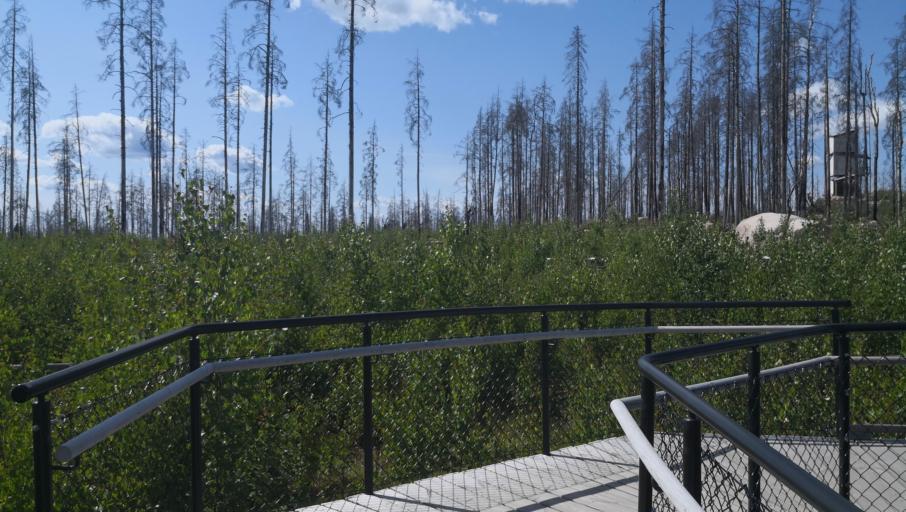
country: SE
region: Vaestmanland
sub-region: Surahammars Kommun
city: Ramnas
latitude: 59.9128
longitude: 16.1494
